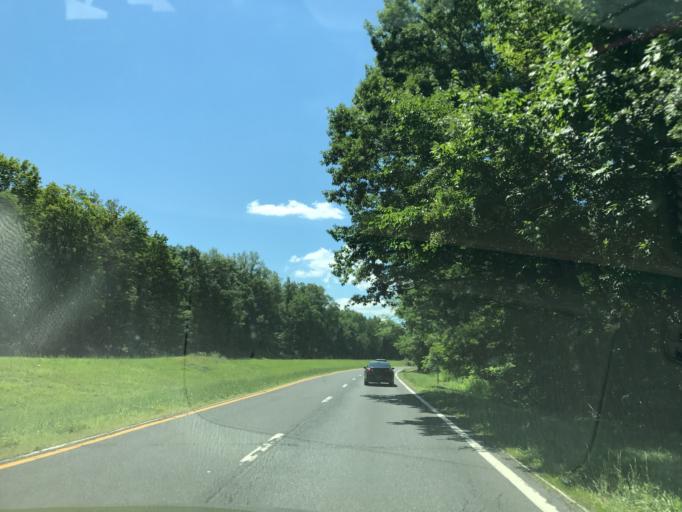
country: US
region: New York
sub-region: Dutchess County
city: Pleasant Valley
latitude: 41.7142
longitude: -73.7833
